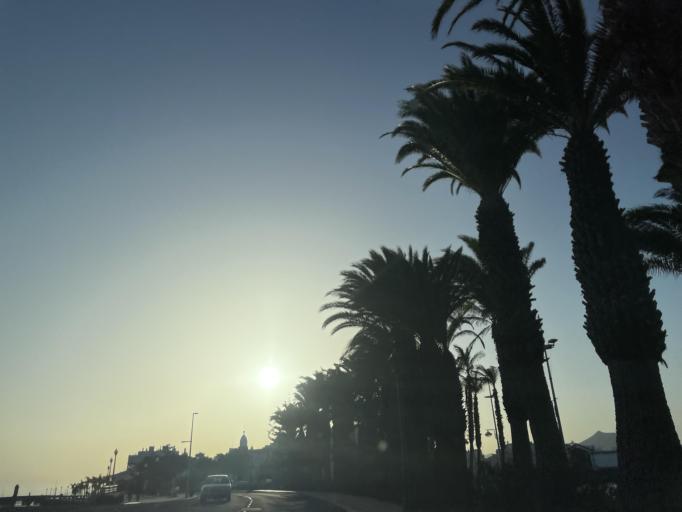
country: ES
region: Canary Islands
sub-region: Provincia de Las Palmas
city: Arrecife
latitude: 28.9606
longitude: -13.5444
